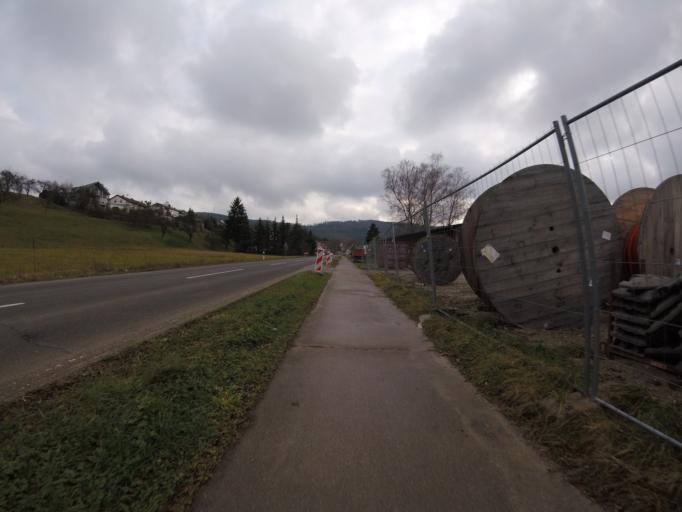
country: DE
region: Baden-Wuerttemberg
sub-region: Regierungsbezirk Stuttgart
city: Allmersbach im Tal
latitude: 48.9111
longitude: 9.4837
